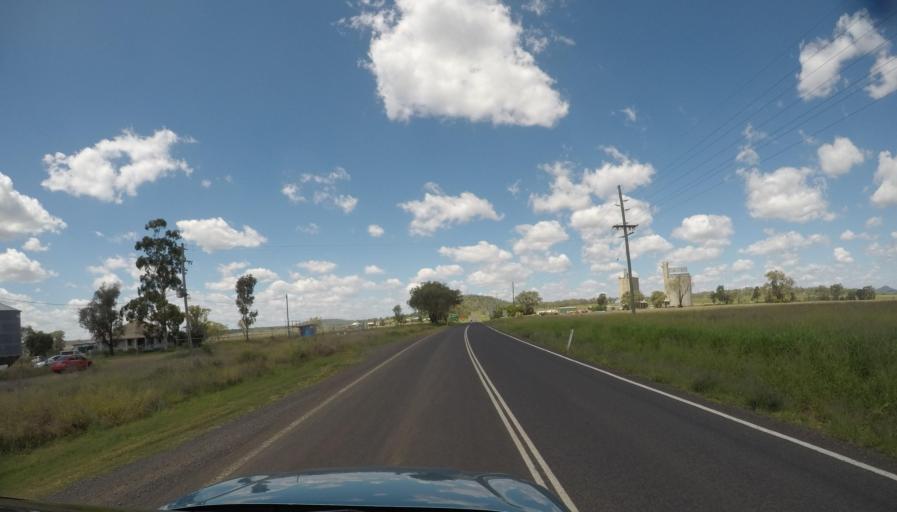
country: AU
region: Queensland
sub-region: Toowoomba
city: Oakey
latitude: -27.5347
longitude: 151.6277
